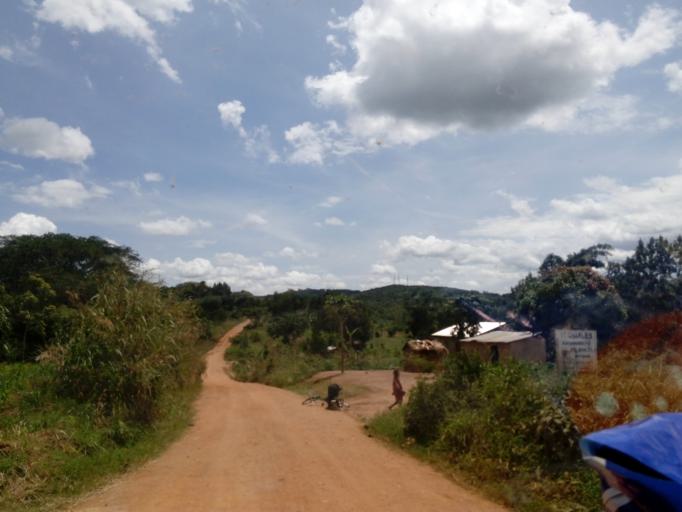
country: UG
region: Central Region
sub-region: Mityana District
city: Mityana
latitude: 0.4622
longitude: 31.7033
